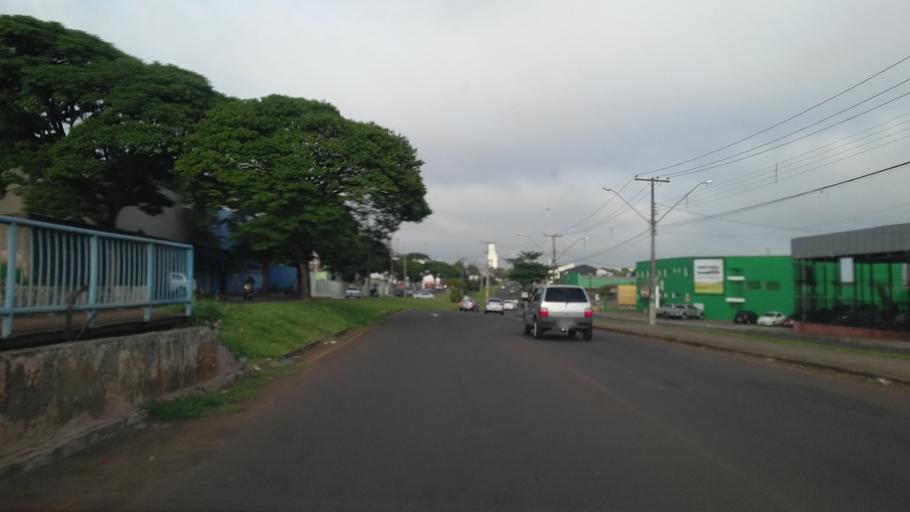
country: BR
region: Parana
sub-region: Londrina
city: Londrina
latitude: -23.2970
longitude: -51.1926
